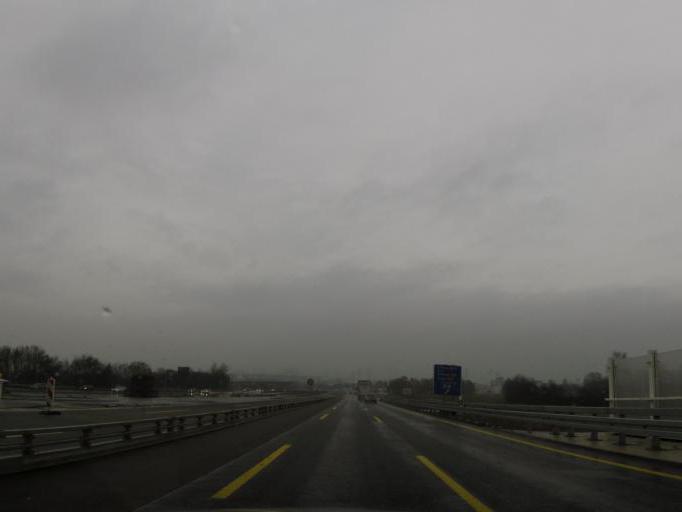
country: DE
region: Hesse
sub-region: Regierungsbezirk Giessen
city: Limburg an der Lahn
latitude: 50.3908
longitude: 8.0795
